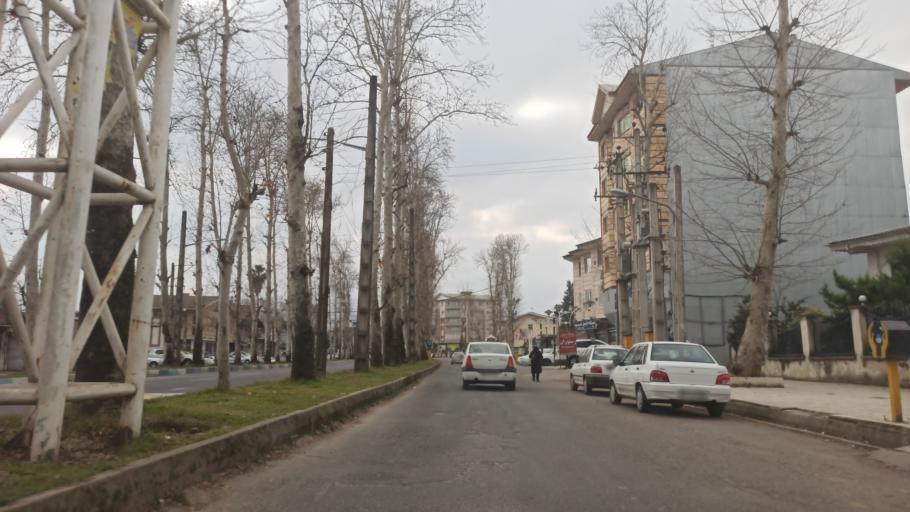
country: IR
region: Gilan
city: Fuman
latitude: 37.2339
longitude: 49.3208
